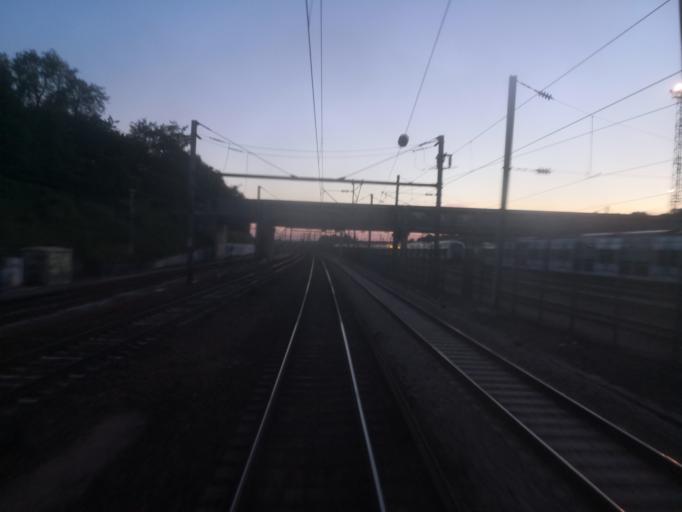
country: FR
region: Ile-de-France
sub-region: Departement des Yvelines
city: Le Mesnil-le-Roi
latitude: 48.9590
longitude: 2.1163
